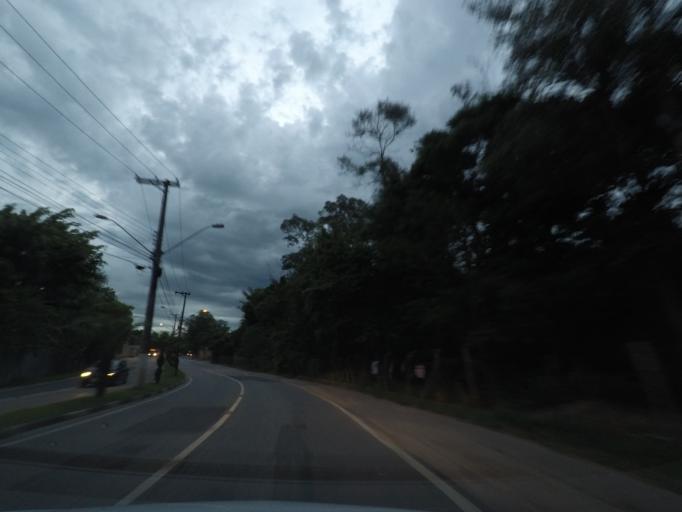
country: BR
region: Sao Paulo
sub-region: Vinhedo
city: Vinhedo
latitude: -23.0348
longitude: -46.9944
